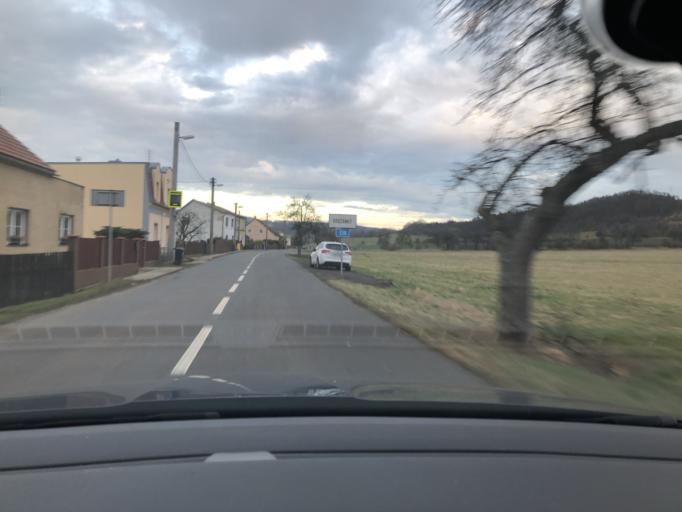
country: CZ
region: Ustecky
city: Rehlovice
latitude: 50.6065
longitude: 13.9329
